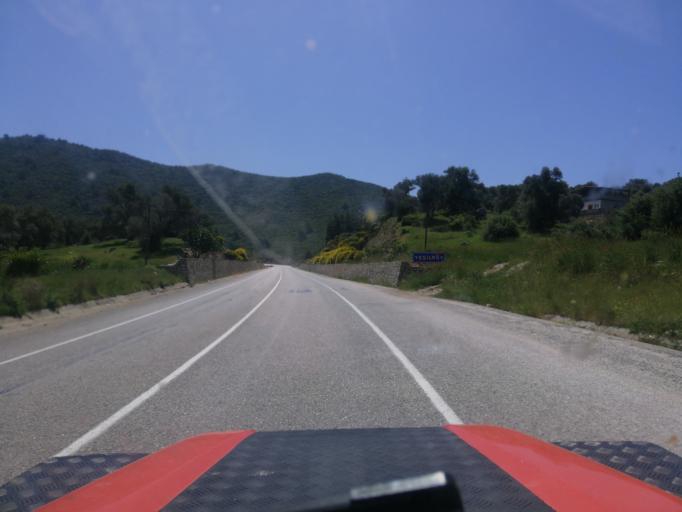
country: TR
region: Antalya
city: Kalkan
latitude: 36.2735
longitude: 29.3626
